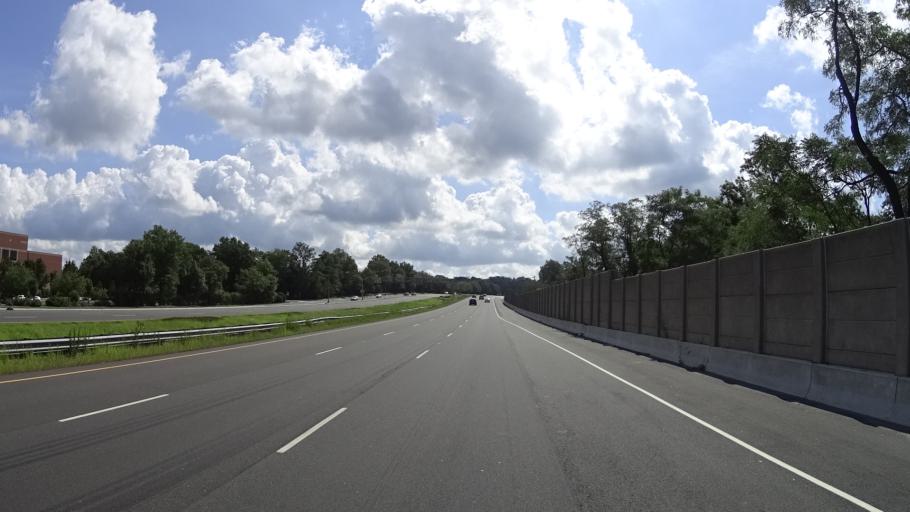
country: US
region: New Jersey
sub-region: Union County
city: Summit
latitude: 40.7376
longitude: -74.3657
